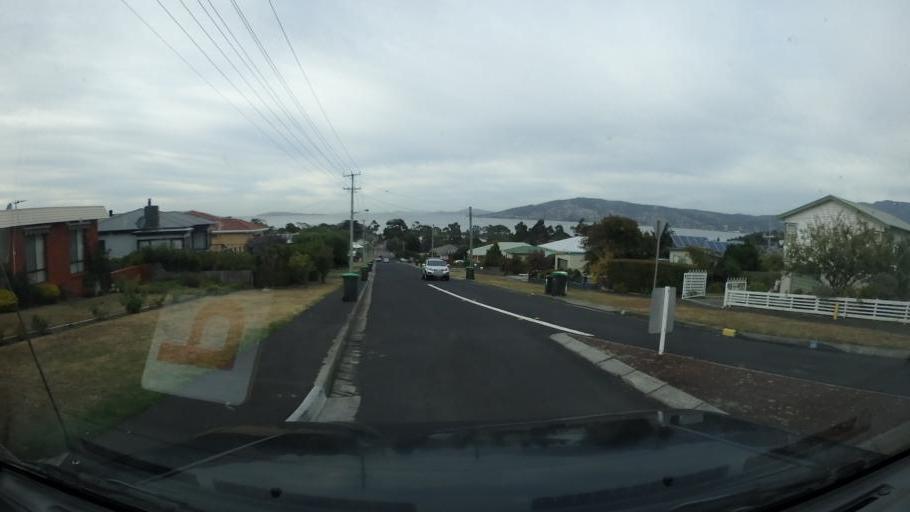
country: AU
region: Tasmania
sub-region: Clarence
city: Bellerive
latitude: -42.8736
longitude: 147.3828
